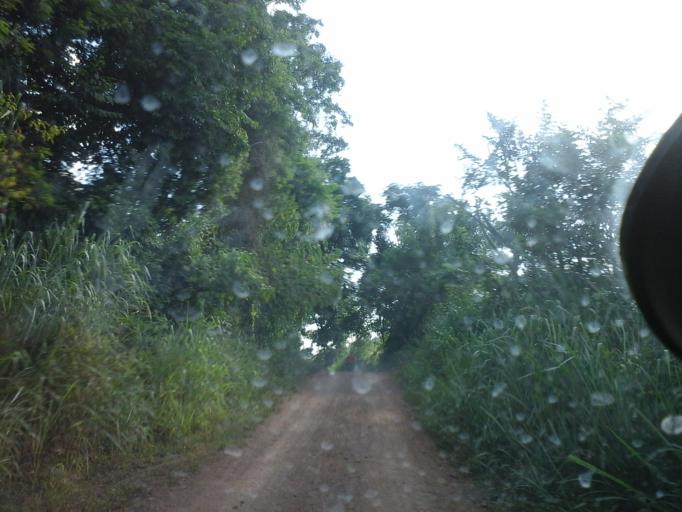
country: CO
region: Cesar
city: San Diego
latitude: 10.2486
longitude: -73.1165
